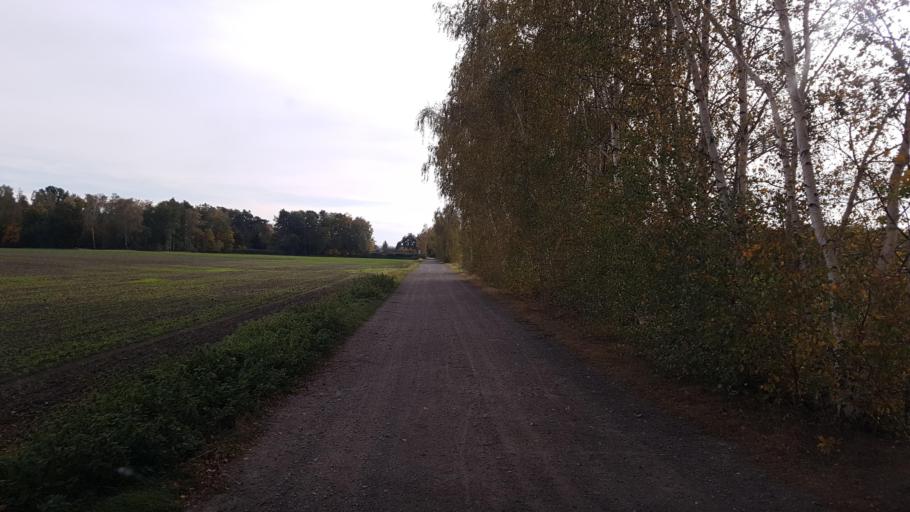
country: DE
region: Brandenburg
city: Schraden
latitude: 51.4446
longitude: 13.6926
